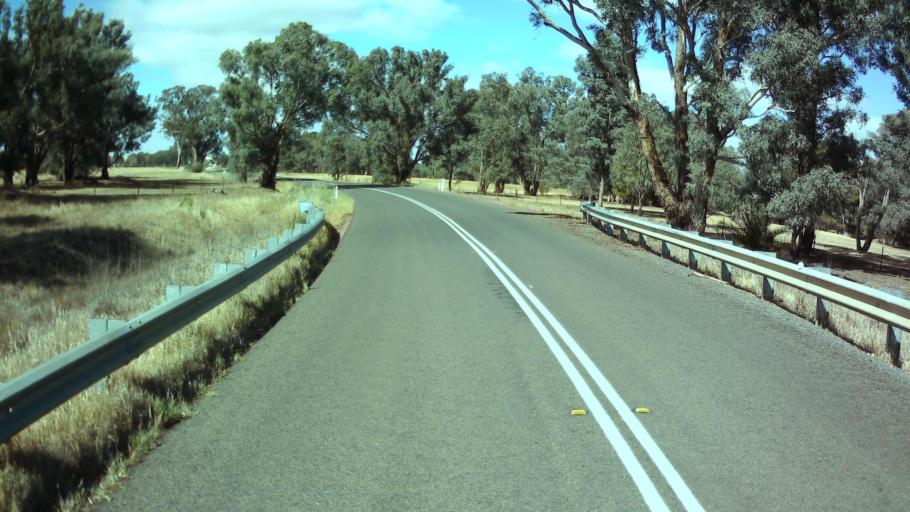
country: AU
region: New South Wales
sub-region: Weddin
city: Grenfell
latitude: -33.9891
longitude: 148.4097
